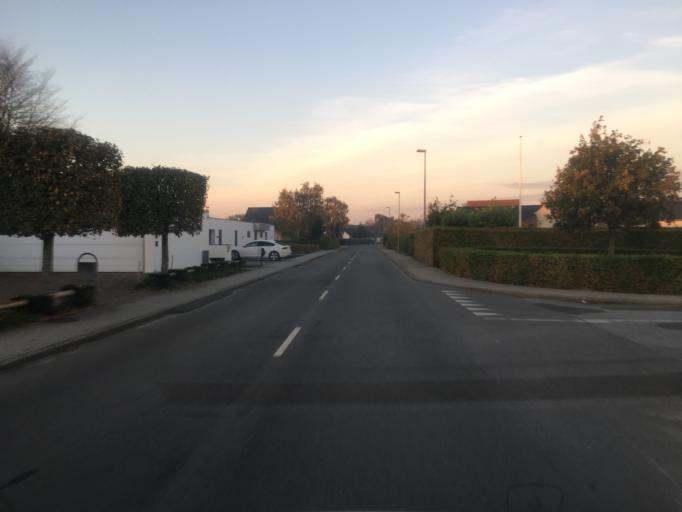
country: DK
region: South Denmark
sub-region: Tonder Kommune
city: Logumkloster
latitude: 55.0594
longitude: 8.9622
